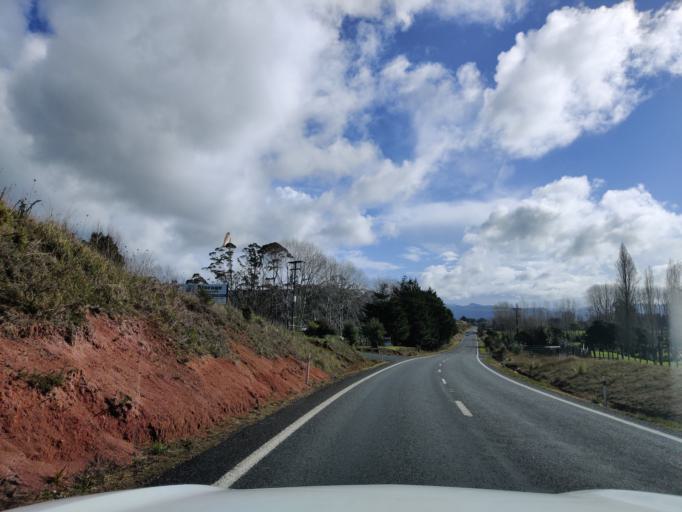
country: NZ
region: Waikato
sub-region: Thames-Coromandel District
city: Whitianga
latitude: -36.7499
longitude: 175.6847
